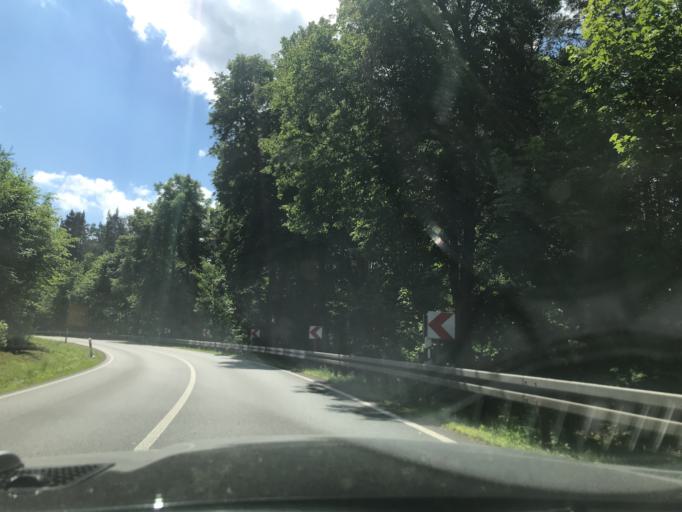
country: DE
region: Thuringia
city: Martinroda
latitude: 50.7070
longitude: 10.8933
